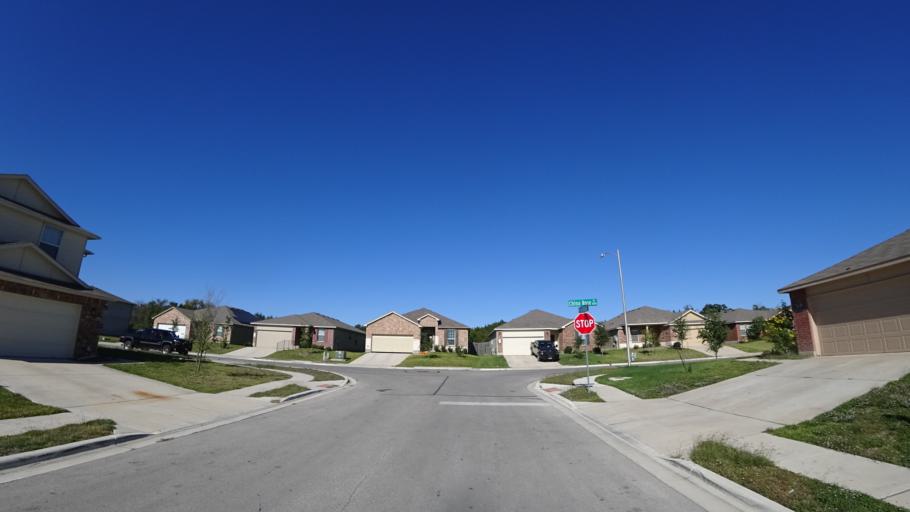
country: US
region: Texas
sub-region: Travis County
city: Hornsby Bend
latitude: 30.2795
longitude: -97.6264
